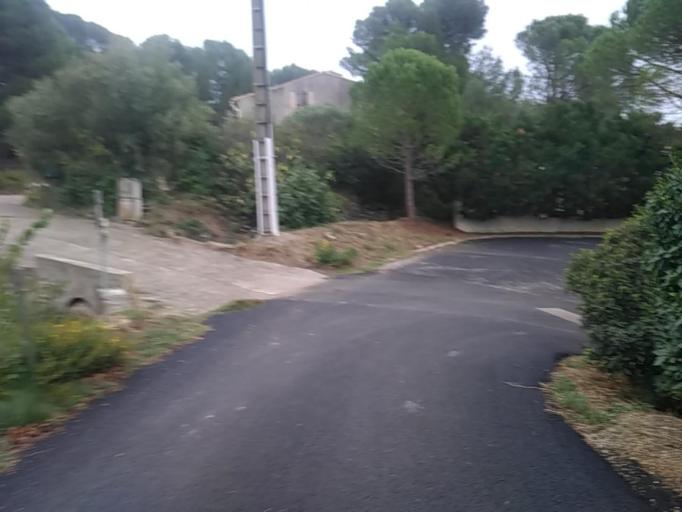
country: FR
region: Languedoc-Roussillon
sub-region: Departement de l'Herault
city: Olonzac
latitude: 43.3255
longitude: 2.7185
